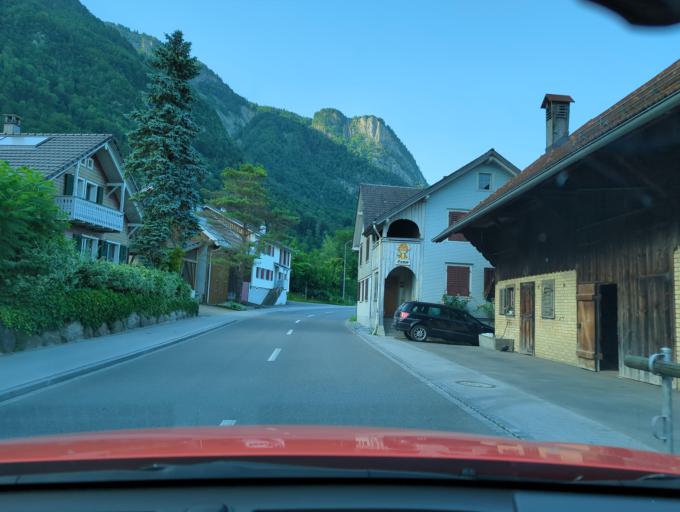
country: CH
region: Saint Gallen
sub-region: Wahlkreis Werdenberg
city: Sennwald
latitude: 47.2476
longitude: 9.4754
